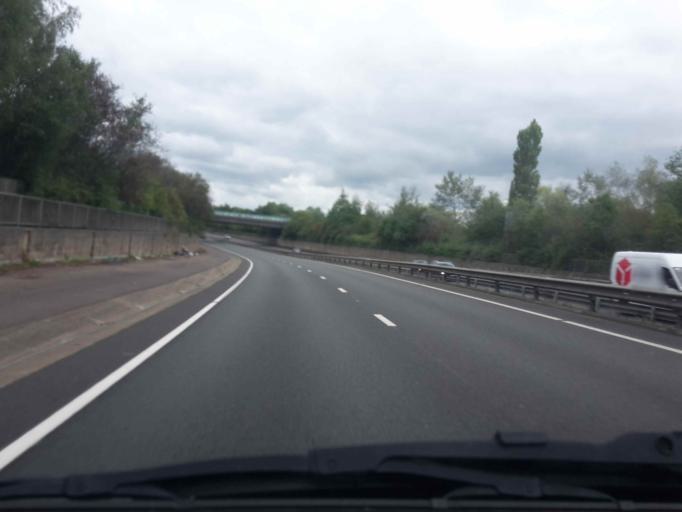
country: GB
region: England
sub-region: Surrey
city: Seale
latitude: 51.2530
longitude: -0.7298
